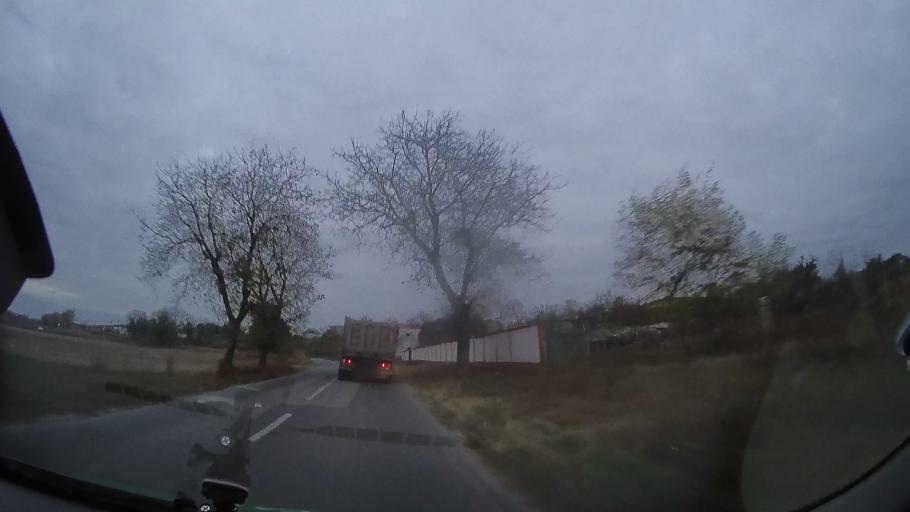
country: RO
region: Tulcea
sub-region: Comuna Mihai Bravu
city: Mihai Bravu
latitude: 44.9548
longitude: 28.6529
